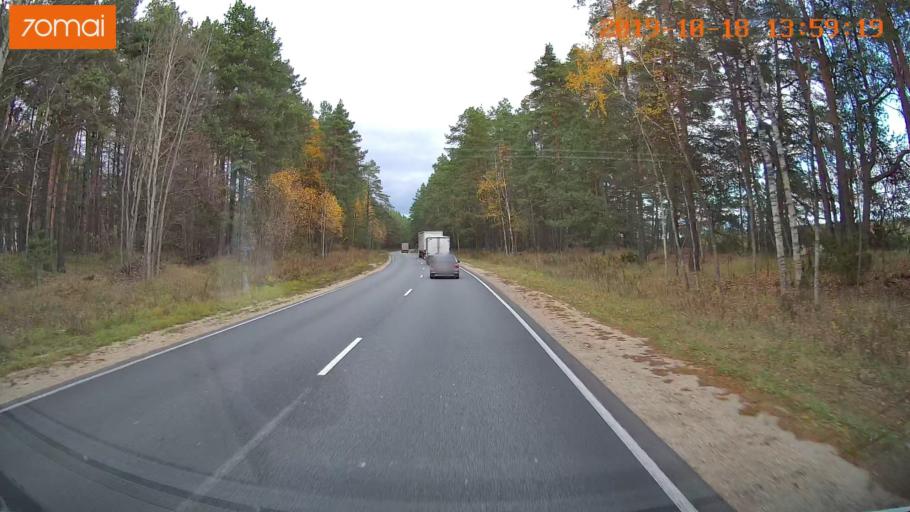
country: RU
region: Rjazan
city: Spas-Klepiki
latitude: 55.0931
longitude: 40.0625
